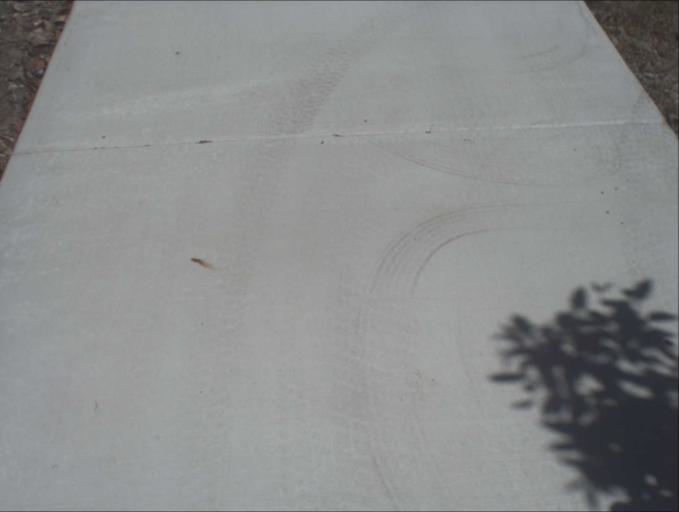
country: AU
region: Queensland
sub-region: Logan
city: Windaroo
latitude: -27.7178
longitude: 153.1665
